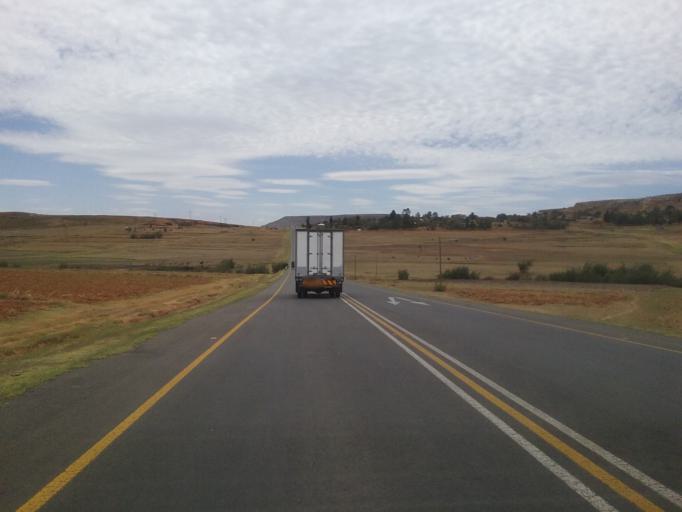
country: LS
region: Maseru
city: Nako
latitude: -29.6393
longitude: 27.4774
